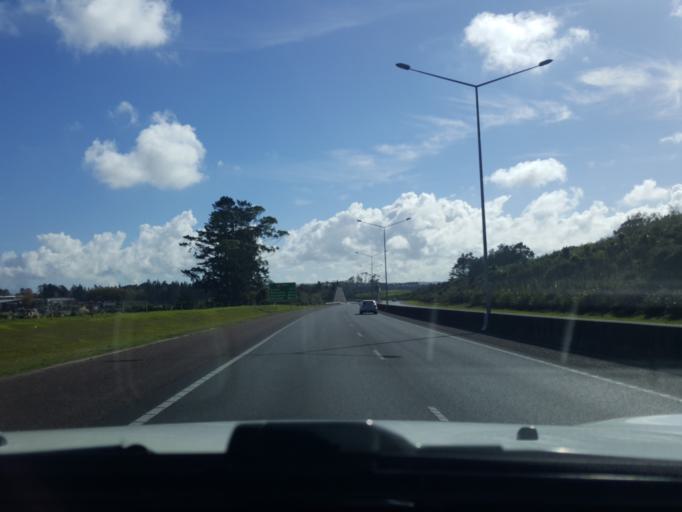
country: NZ
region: Auckland
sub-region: Auckland
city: Rosebank
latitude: -36.8115
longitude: 174.6106
